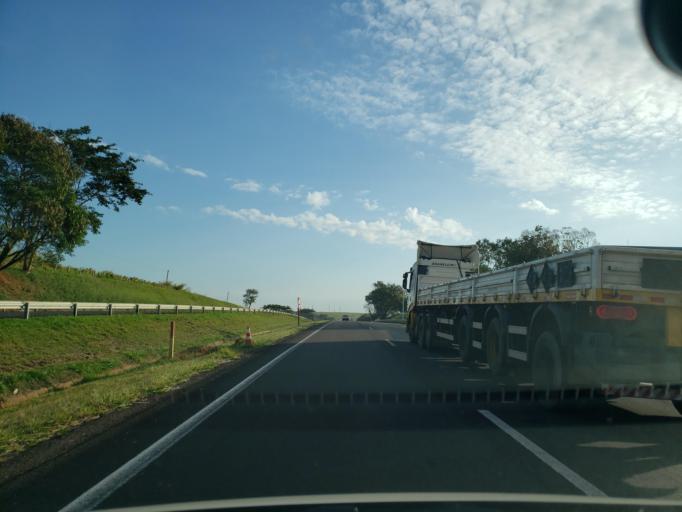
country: BR
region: Sao Paulo
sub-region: Valparaiso
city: Valparaiso
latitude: -21.2118
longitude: -50.8295
